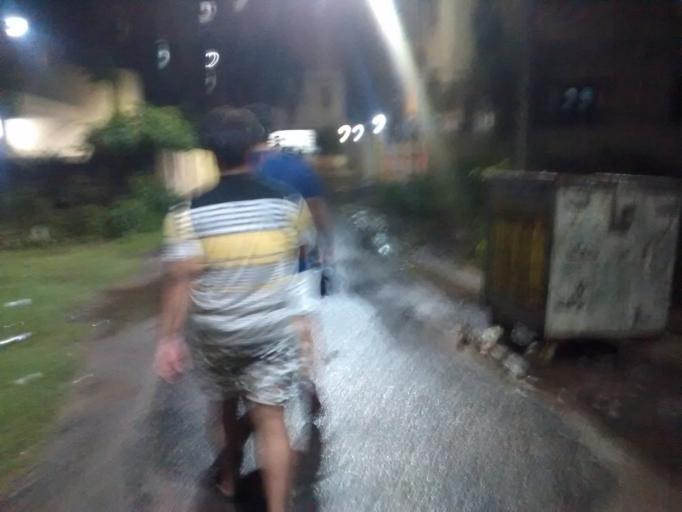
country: IN
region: Tamil Nadu
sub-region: Kancheepuram
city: Perungudi
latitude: 12.9460
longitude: 80.2366
